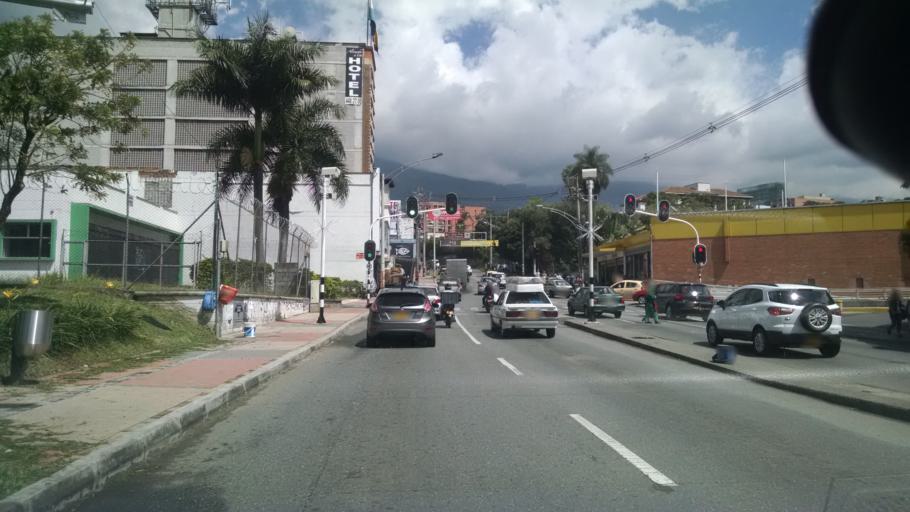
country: CO
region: Antioquia
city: Itagui
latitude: 6.2128
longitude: -75.5750
